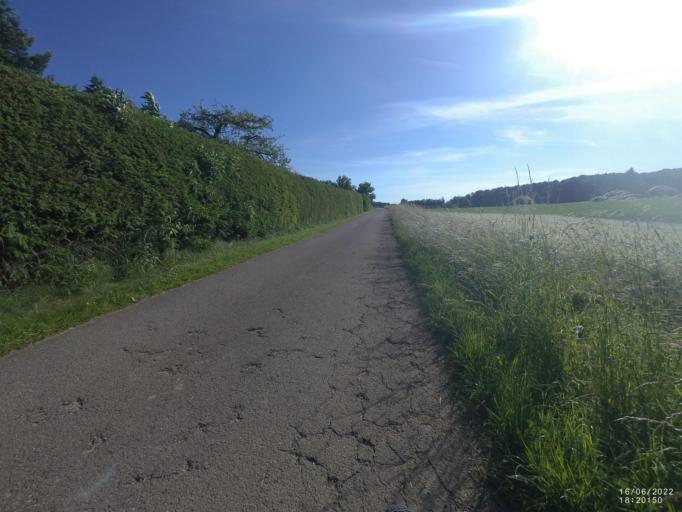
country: DE
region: Baden-Wuerttemberg
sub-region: Regierungsbezirk Stuttgart
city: Gerstetten
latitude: 48.6107
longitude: 10.0402
